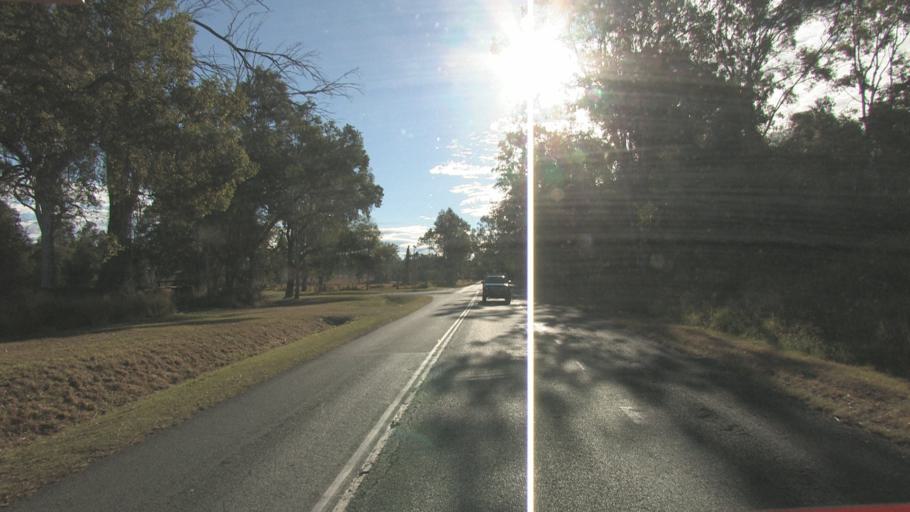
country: AU
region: Queensland
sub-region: Logan
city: Cedar Vale
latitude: -27.8858
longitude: 153.0790
